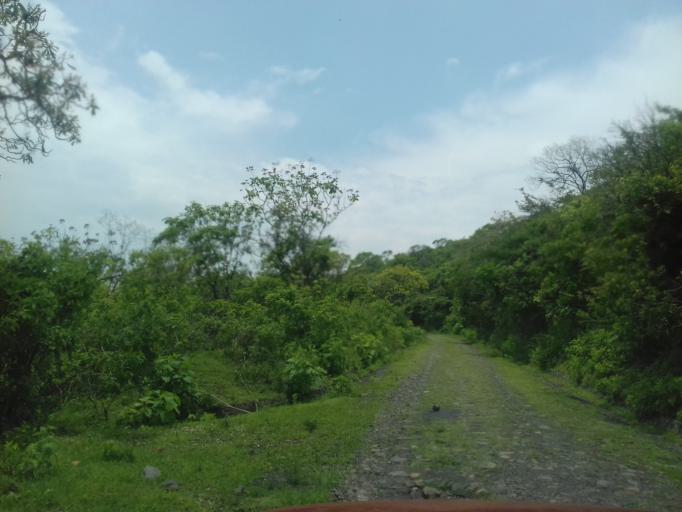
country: MX
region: Nayarit
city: Jala
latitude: 21.1107
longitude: -104.4875
